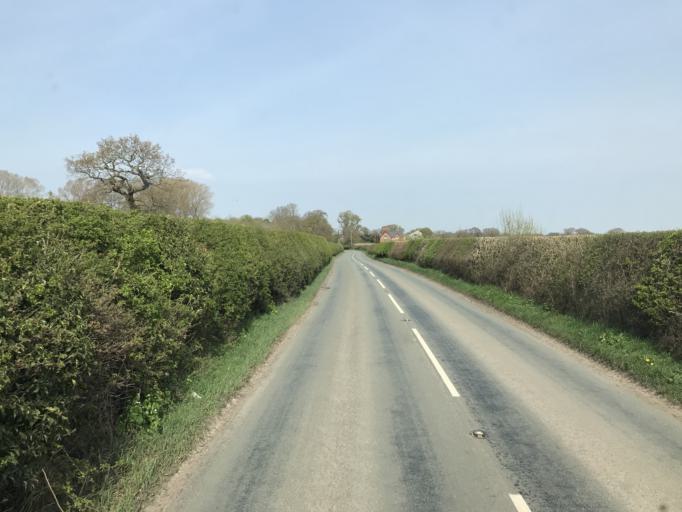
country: GB
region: England
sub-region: Cheshire West and Chester
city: Aldford
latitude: 53.1436
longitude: -2.8622
